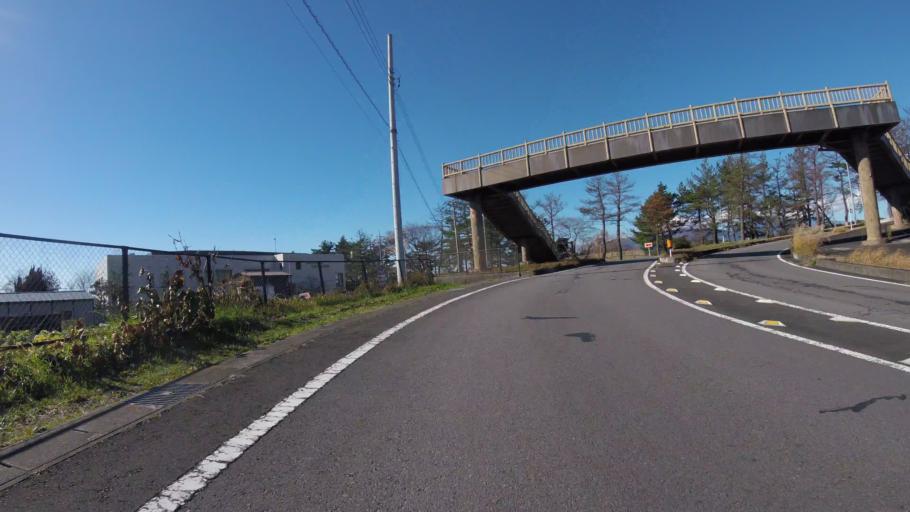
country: JP
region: Shizuoka
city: Mishima
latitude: 35.1270
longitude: 138.9407
